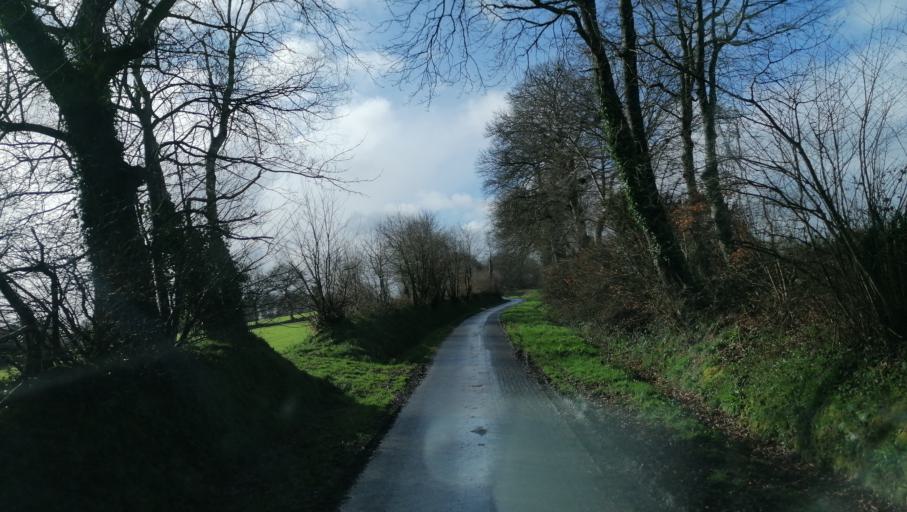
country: FR
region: Brittany
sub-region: Departement des Cotes-d'Armor
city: Lanrodec
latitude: 48.4929
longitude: -3.0193
